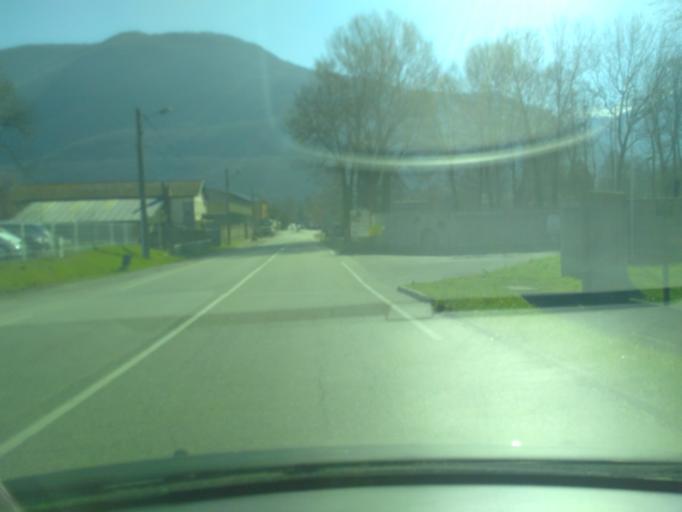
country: FR
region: Rhone-Alpes
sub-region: Departement de l'Isere
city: Notre-Dame-de-Mesage
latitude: 45.0696
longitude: 5.7644
